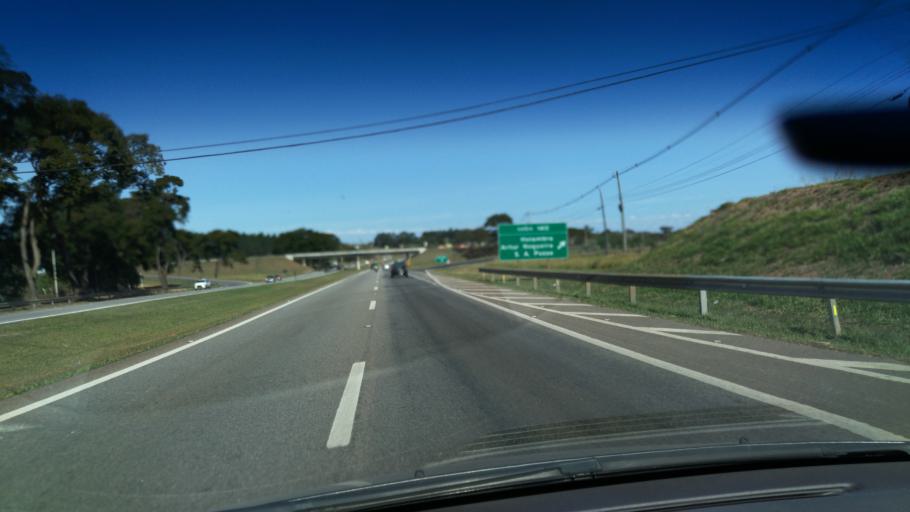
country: BR
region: Sao Paulo
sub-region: Santo Antonio De Posse
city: Santo Antonio de Posse
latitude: -22.6175
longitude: -47.0072
